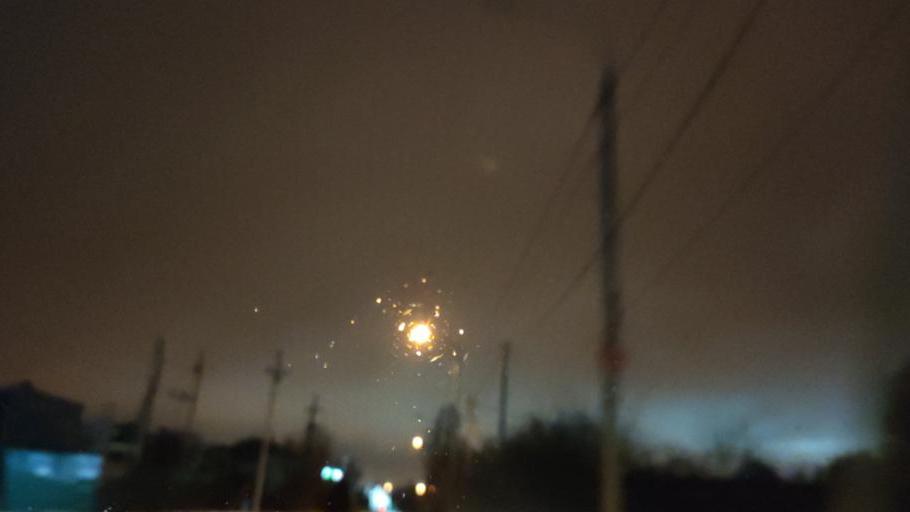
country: RU
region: Moskovskaya
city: Annino
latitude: 55.5721
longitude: 37.2681
